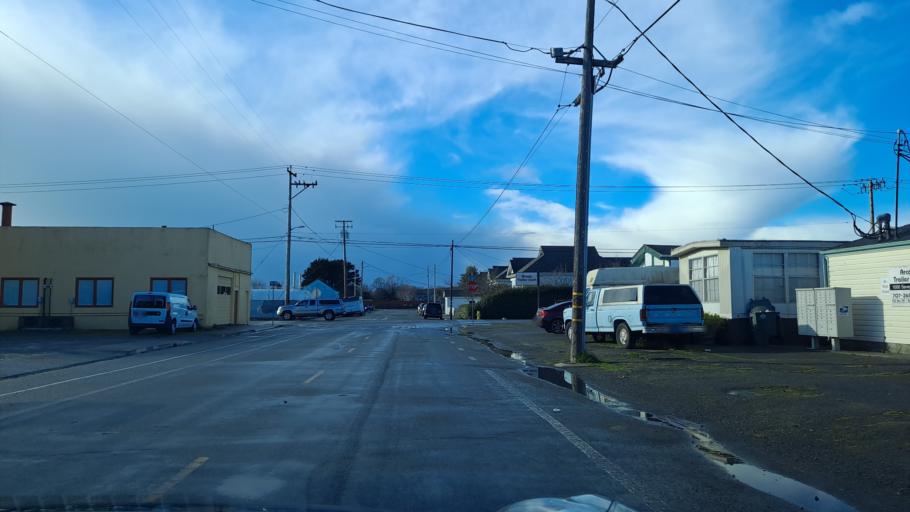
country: US
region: California
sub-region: Humboldt County
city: Arcata
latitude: 40.8680
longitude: -124.0899
